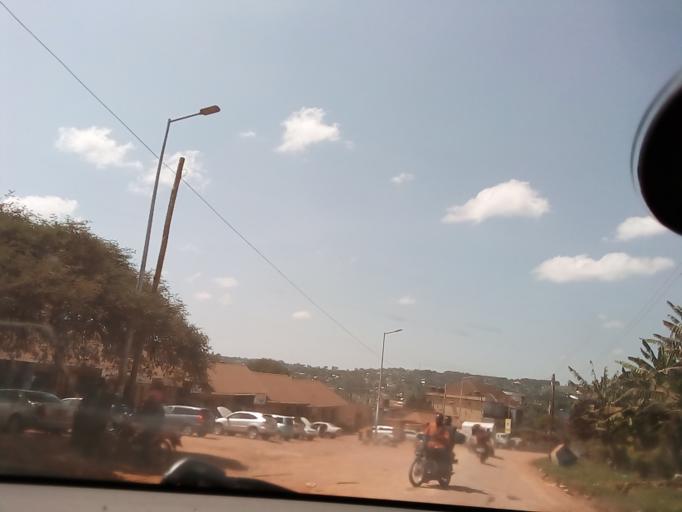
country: UG
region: Central Region
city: Masaka
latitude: -0.3324
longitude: 31.7419
